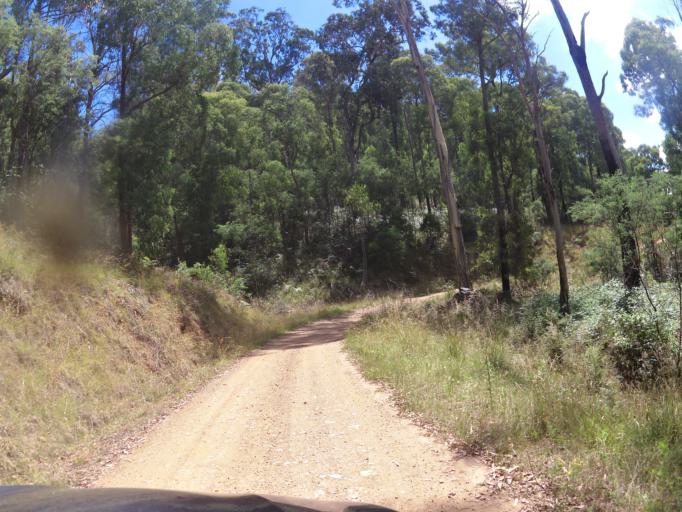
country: AU
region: Victoria
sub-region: Alpine
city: Mount Beauty
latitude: -36.7976
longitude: 147.0889
